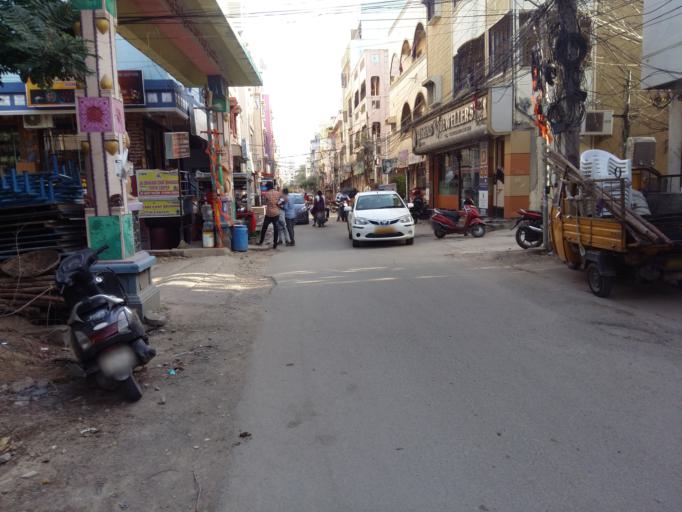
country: IN
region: Telangana
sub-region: Rangareddi
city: Kukatpalli
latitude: 17.4905
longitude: 78.3993
